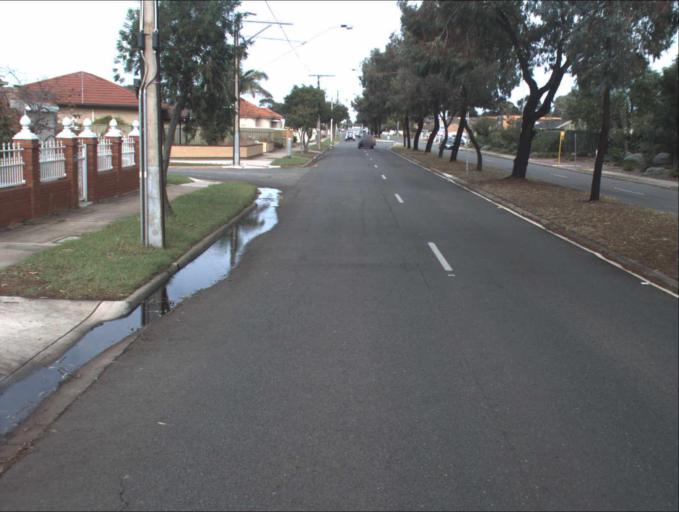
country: AU
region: South Australia
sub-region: Charles Sturt
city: Royal Park
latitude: -34.8753
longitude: 138.5036
